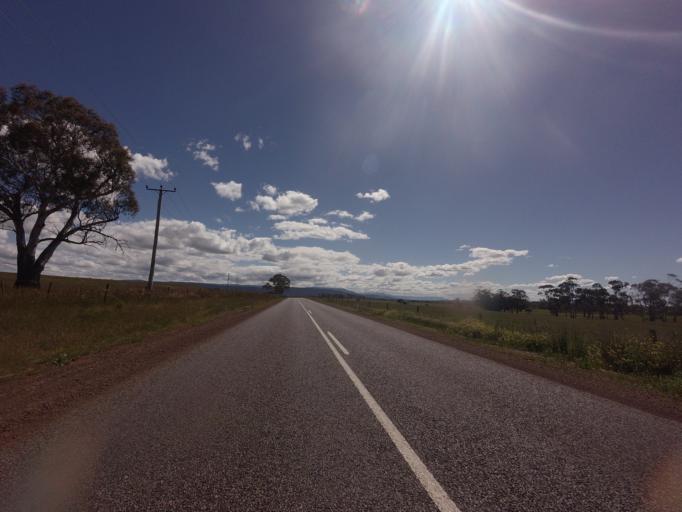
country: AU
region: Tasmania
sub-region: Northern Midlands
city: Evandale
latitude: -41.9431
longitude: 147.5311
